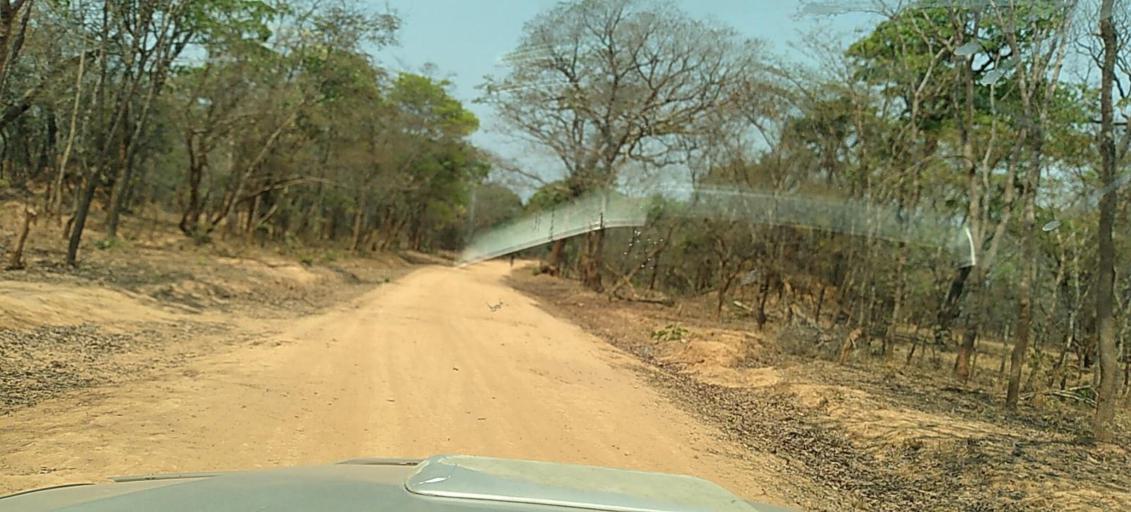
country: ZM
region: North-Western
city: Kasempa
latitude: -13.6647
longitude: 26.2813
